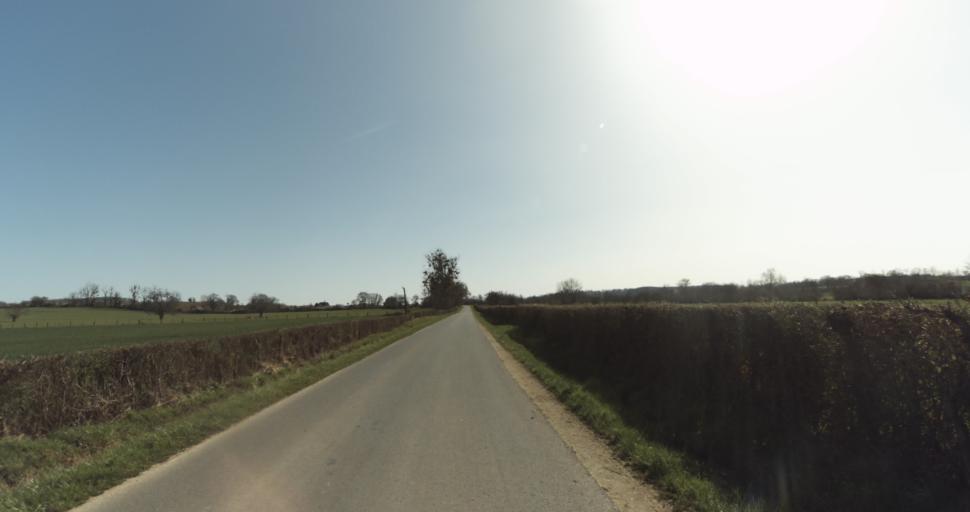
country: FR
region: Lower Normandy
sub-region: Departement de l'Orne
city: Trun
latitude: 48.9260
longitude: 0.0299
